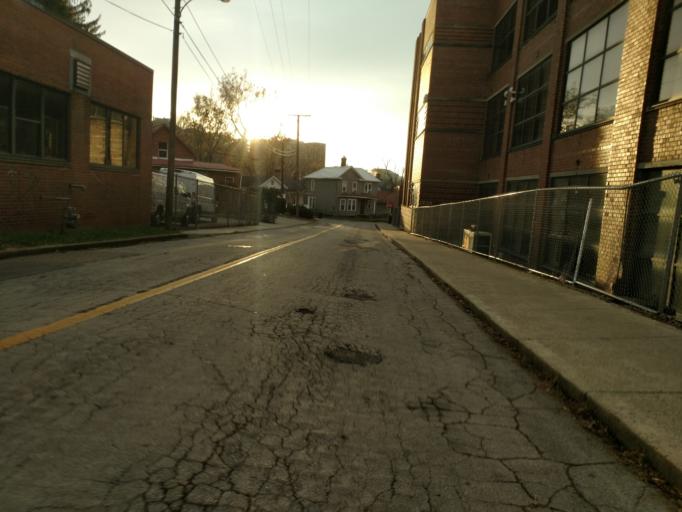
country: US
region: Ohio
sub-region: Athens County
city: Athens
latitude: 39.3307
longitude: -82.1078
